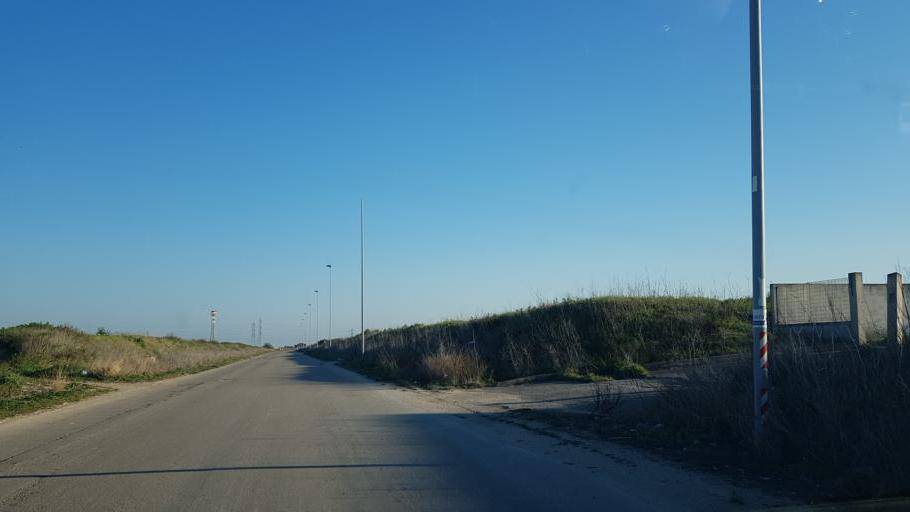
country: IT
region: Apulia
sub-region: Provincia di Brindisi
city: La Rosa
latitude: 40.6222
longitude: 17.9697
